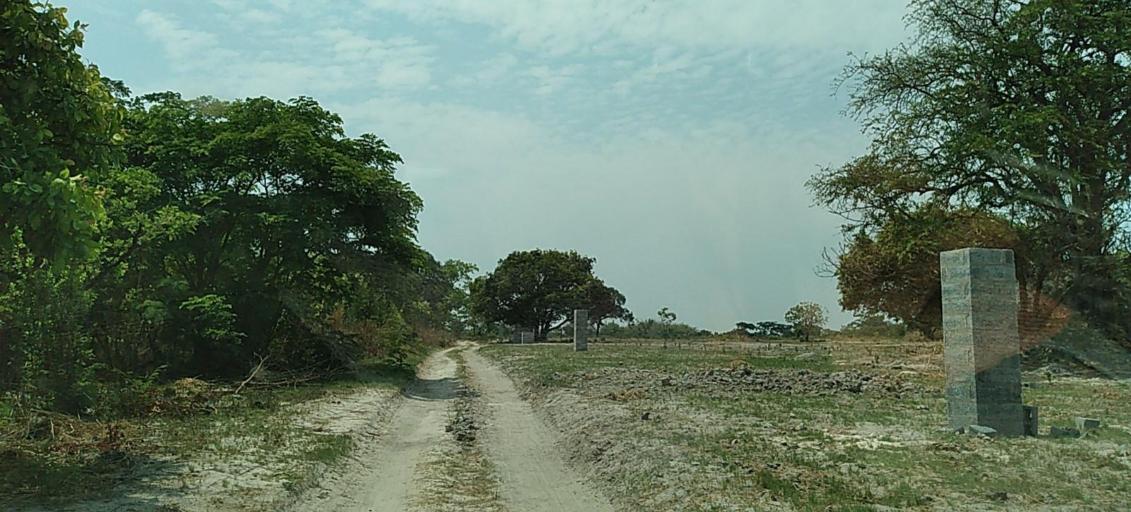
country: ZM
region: Copperbelt
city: Kalulushi
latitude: -12.9380
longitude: 28.1153
